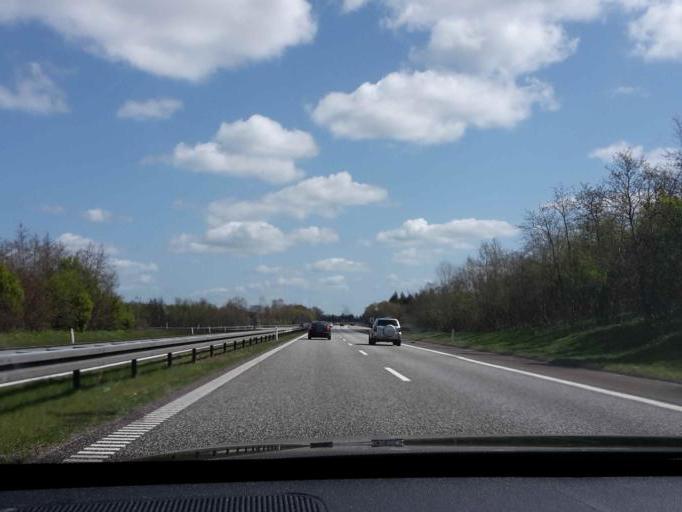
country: DK
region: South Denmark
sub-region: Vejen Kommune
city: Vejen
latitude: 55.4945
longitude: 9.1307
